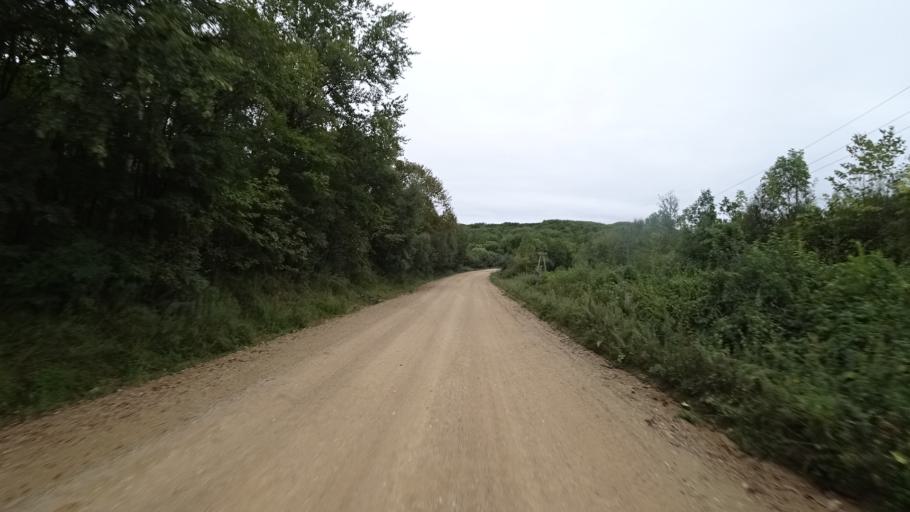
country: RU
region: Primorskiy
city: Rettikhovka
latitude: 44.1755
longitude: 132.8365
